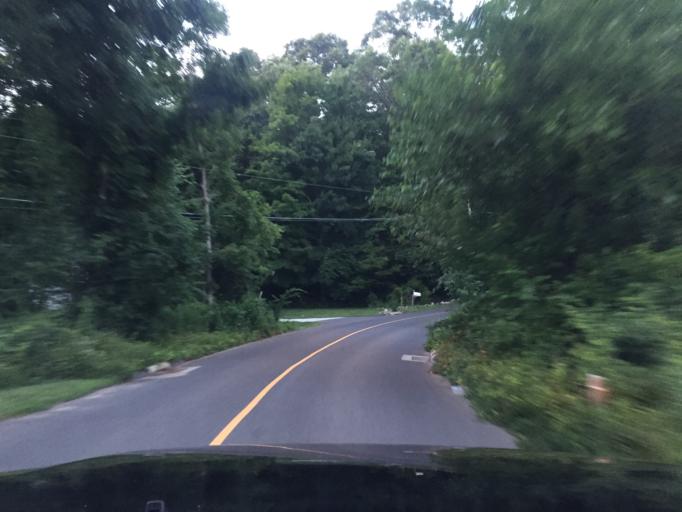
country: US
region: Connecticut
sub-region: Fairfield County
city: Bethel
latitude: 41.4087
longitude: -73.3765
